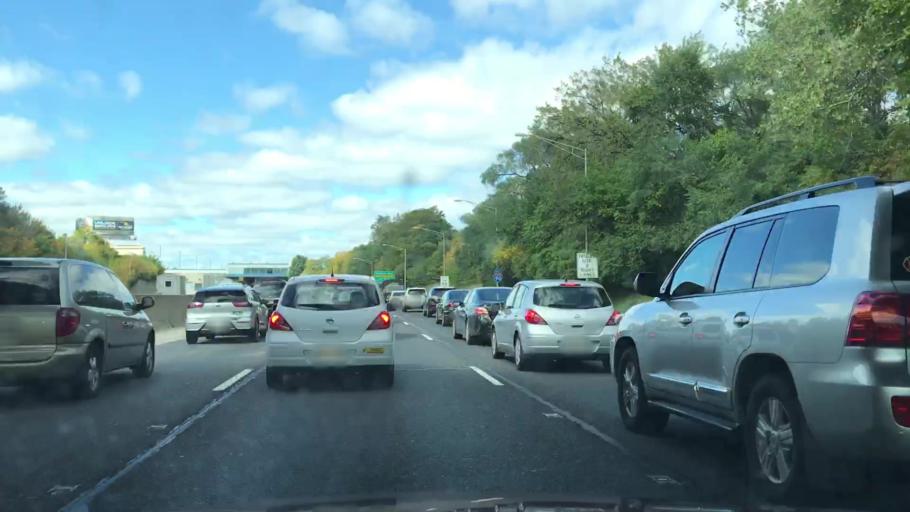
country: US
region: Illinois
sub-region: Cook County
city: Harwood Heights
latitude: 41.9688
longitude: -87.7610
